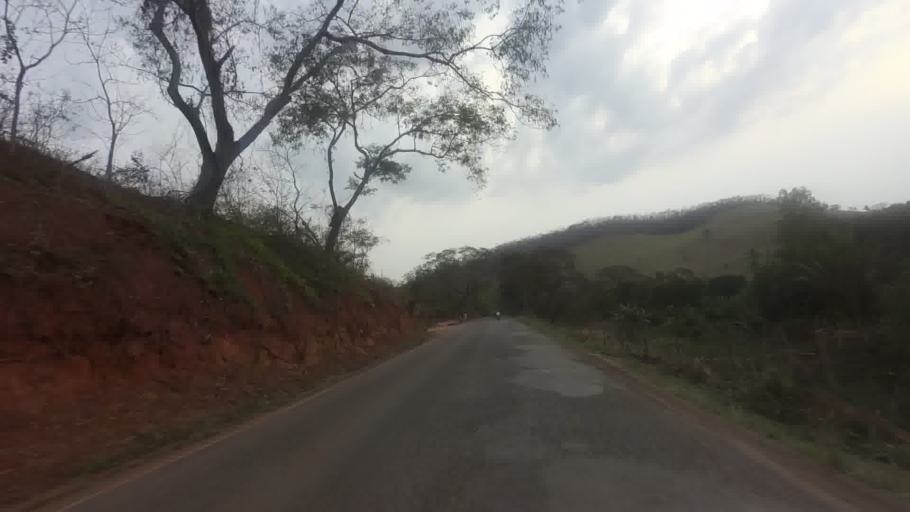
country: BR
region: Rio de Janeiro
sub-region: Santo Antonio De Padua
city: Santo Antonio de Padua
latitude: -21.5237
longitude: -42.1075
